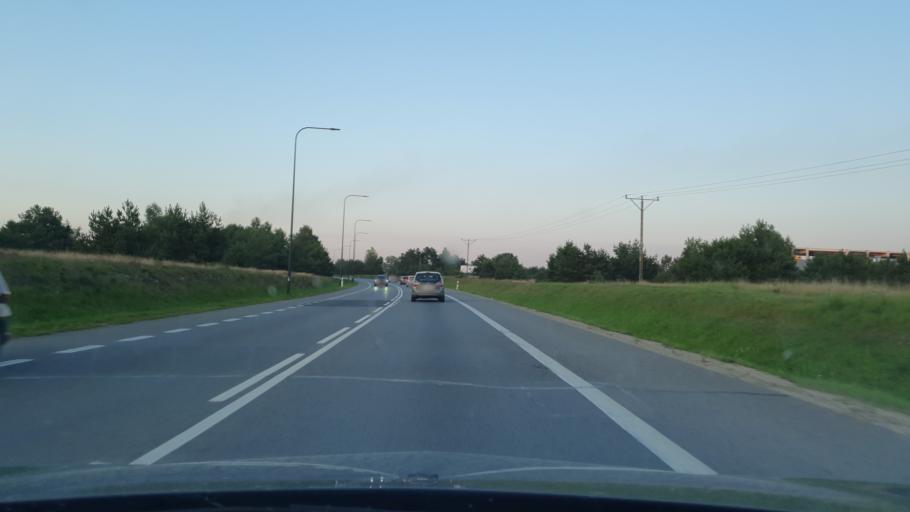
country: PL
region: Pomeranian Voivodeship
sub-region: Powiat leborski
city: Lebork
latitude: 54.5411
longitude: 17.7826
